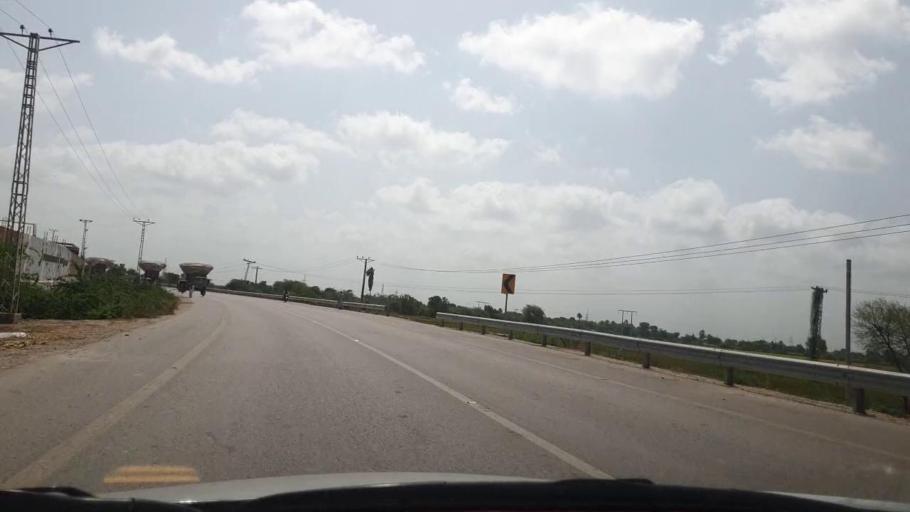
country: PK
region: Sindh
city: Talhar
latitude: 24.8885
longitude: 68.7995
